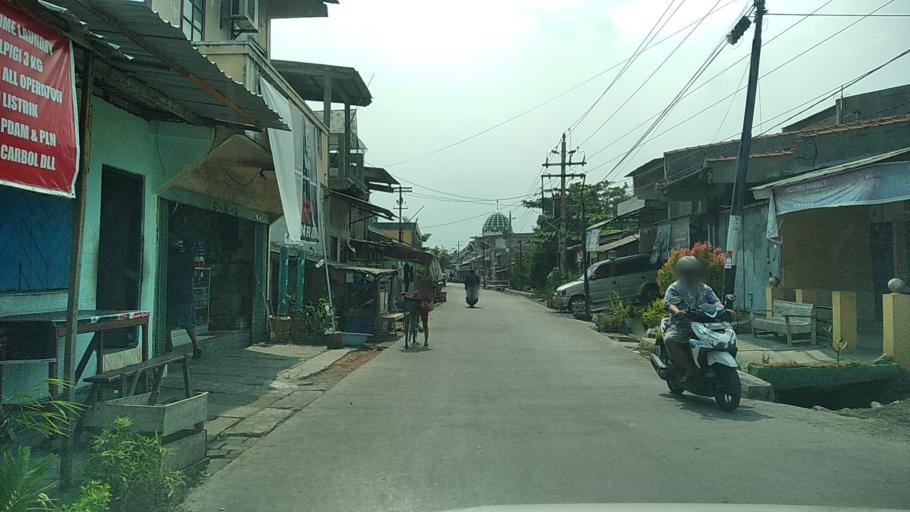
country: ID
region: Central Java
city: Semarang
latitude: -6.9646
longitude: 110.4211
